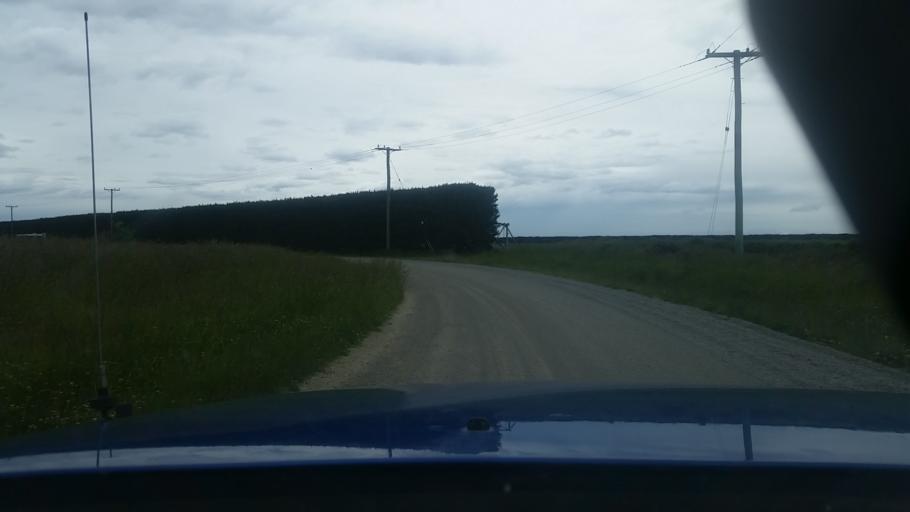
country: NZ
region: Canterbury
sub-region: Ashburton District
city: Rakaia
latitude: -43.9185
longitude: 172.0965
